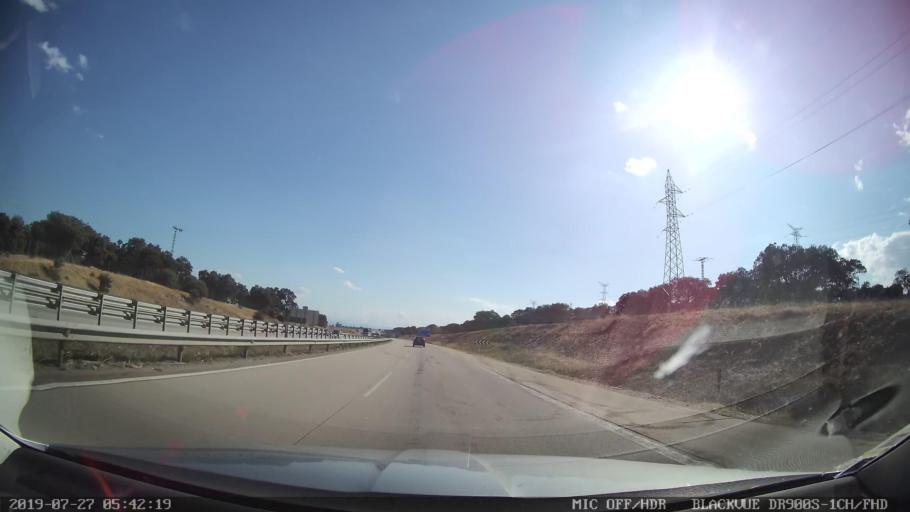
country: ES
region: Castille-La Mancha
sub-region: Province of Toledo
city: Mejorada
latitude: 39.9700
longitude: -4.8924
